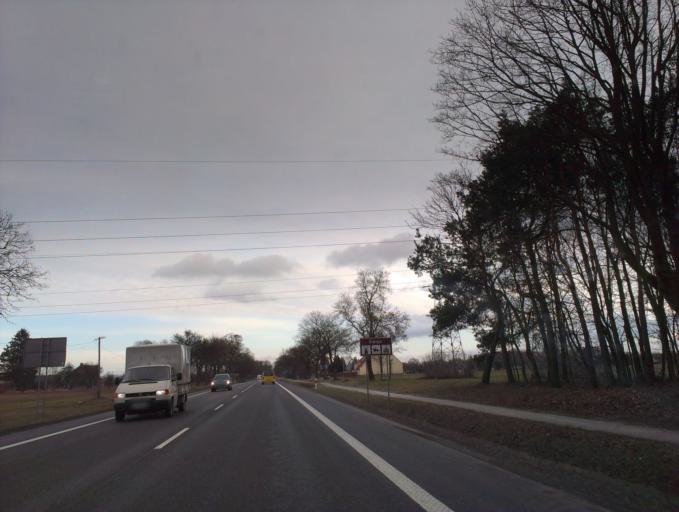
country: PL
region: Masovian Voivodeship
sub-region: Powiat sierpecki
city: Sierpc
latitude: 52.8670
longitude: 19.6540
